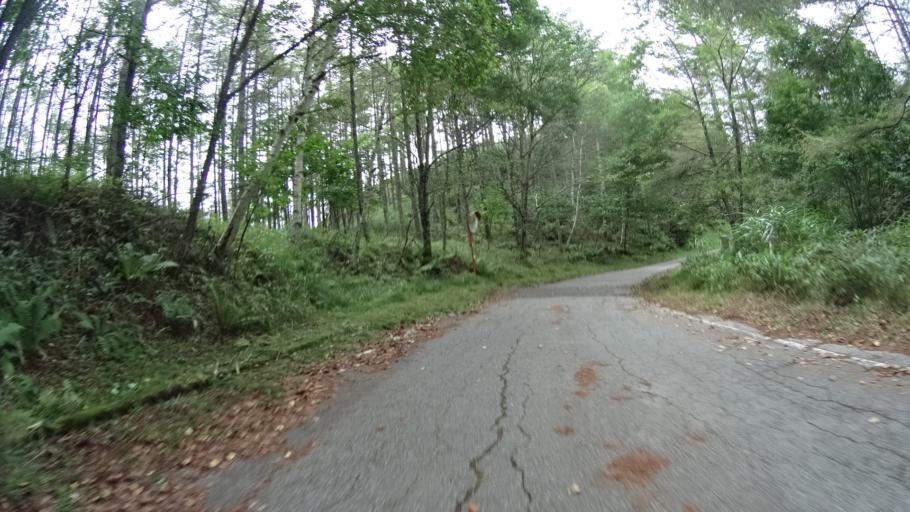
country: JP
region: Yamanashi
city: Kofu-shi
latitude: 35.8289
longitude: 138.5583
